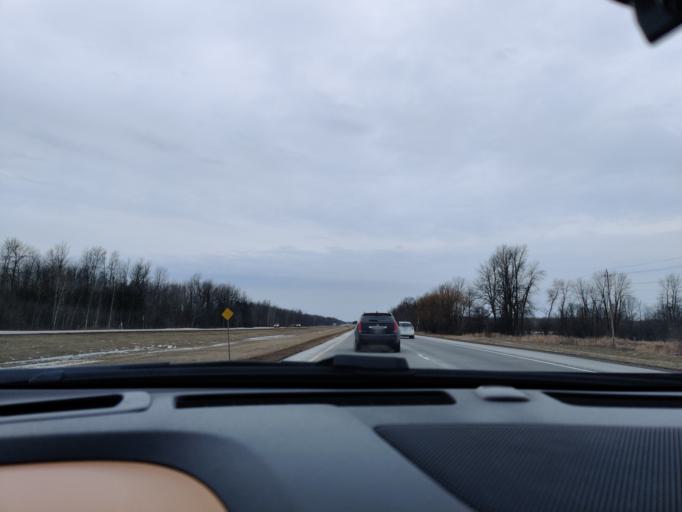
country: US
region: New York
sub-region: St. Lawrence County
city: Norfolk
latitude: 44.9351
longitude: -75.1559
